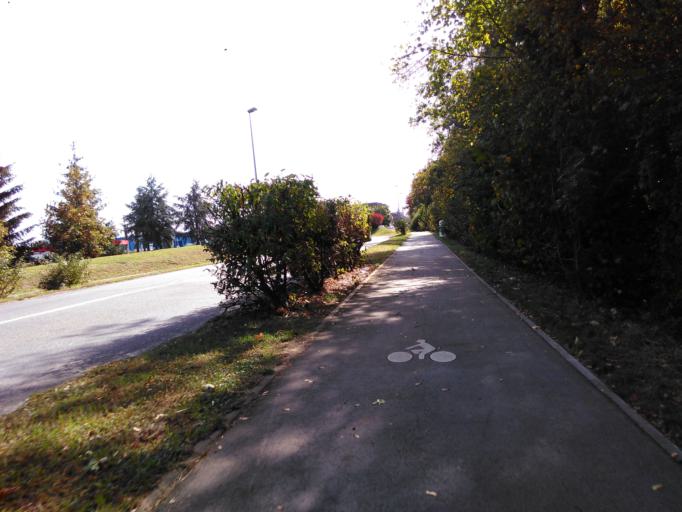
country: FR
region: Lorraine
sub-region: Departement de la Moselle
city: Thionville
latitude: 49.3798
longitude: 6.1693
